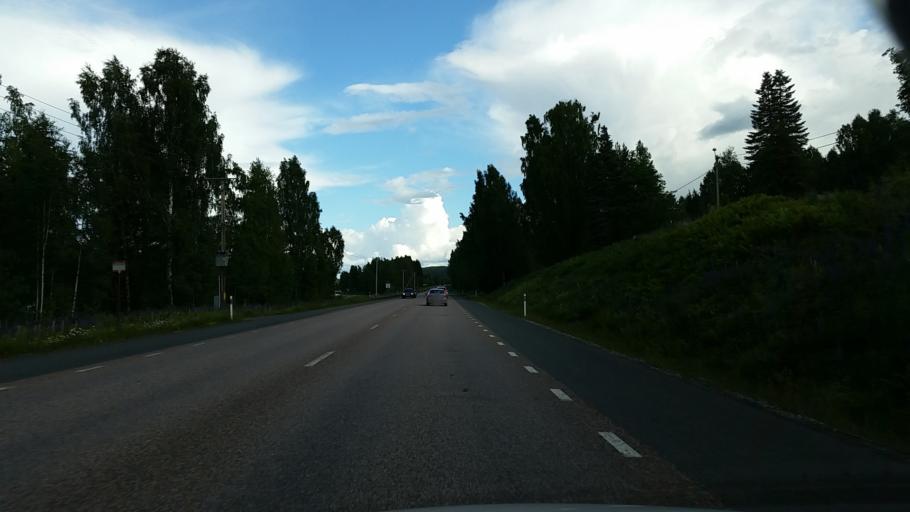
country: SE
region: Vaestmanland
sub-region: Fagersta Kommun
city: Fagersta
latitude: 60.0034
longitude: 15.6583
